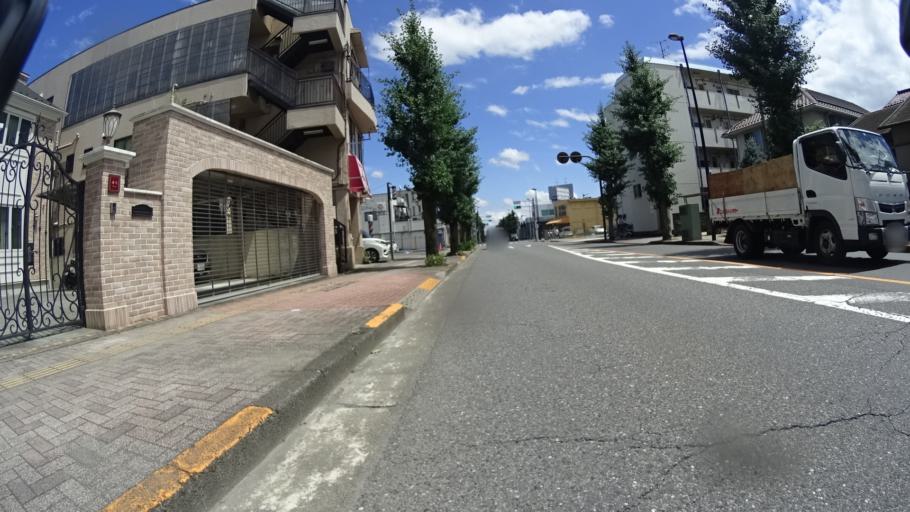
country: JP
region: Tokyo
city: Ome
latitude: 35.7833
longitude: 139.2833
